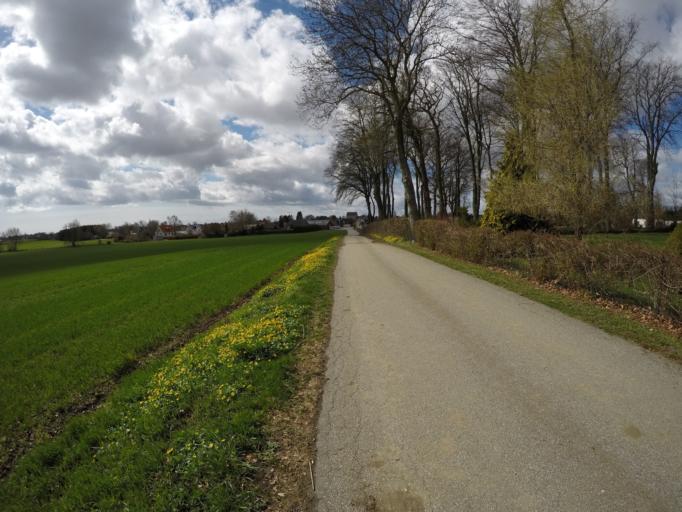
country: SE
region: Skane
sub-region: Ystads Kommun
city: Kopingebro
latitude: 55.4401
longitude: 14.1171
